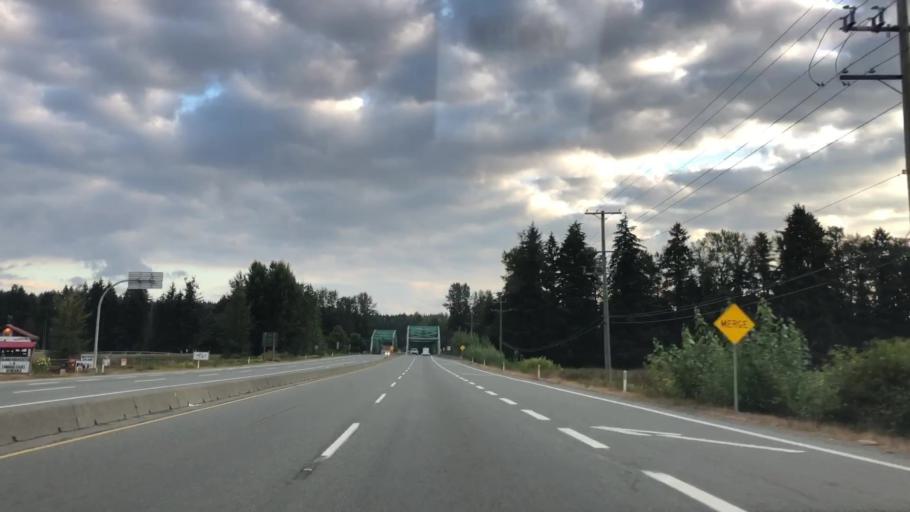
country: CA
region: British Columbia
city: North Cowichan
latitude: 48.8755
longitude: -123.7064
